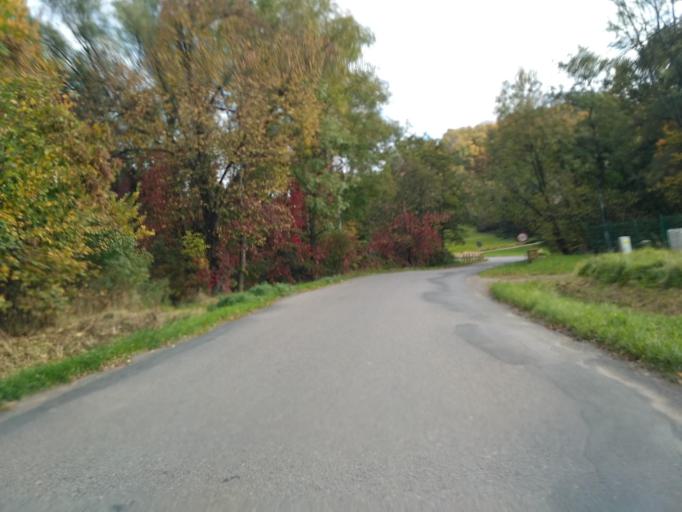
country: PL
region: Subcarpathian Voivodeship
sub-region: Powiat debicki
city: Jodlowa
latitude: 49.8927
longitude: 21.3322
